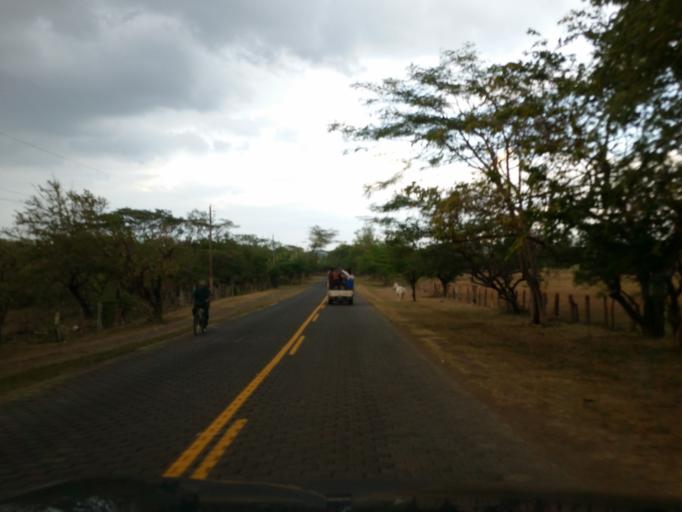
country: NI
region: Managua
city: Carlos Fonseca Amador
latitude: 12.0522
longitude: -86.5069
